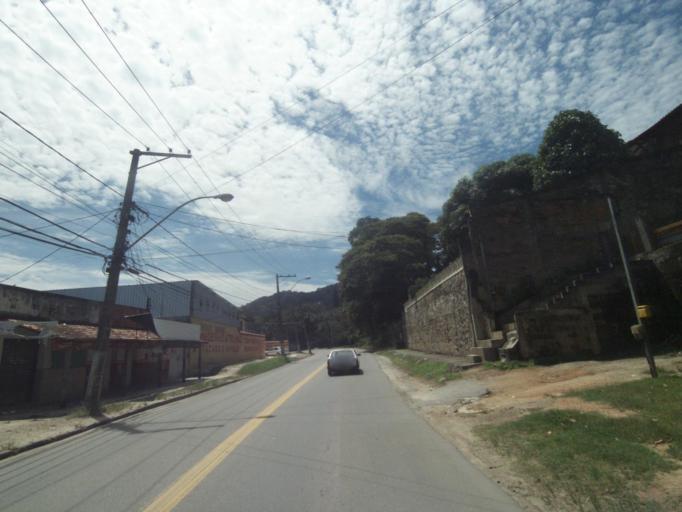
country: BR
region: Rio de Janeiro
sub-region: Niteroi
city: Niteroi
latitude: -22.9309
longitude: -43.0087
